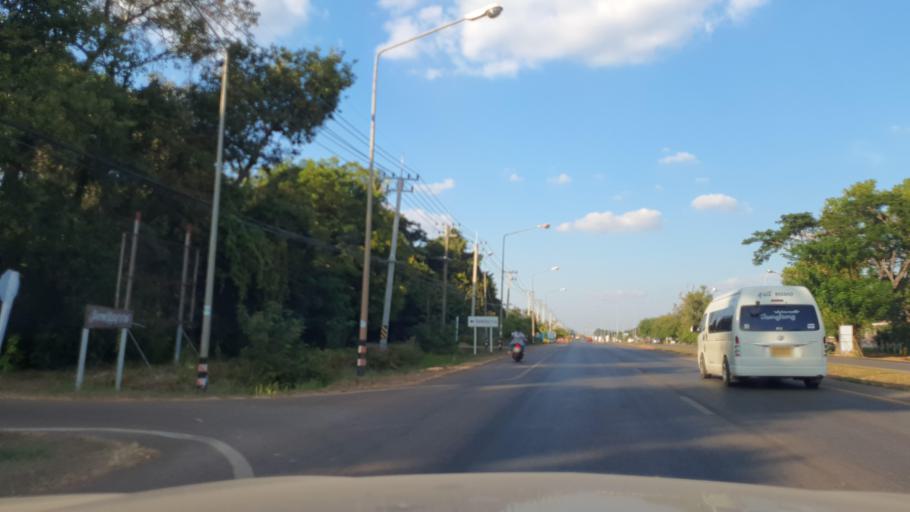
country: TH
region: Sakon Nakhon
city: Sakon Nakhon
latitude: 17.2188
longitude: 104.1043
